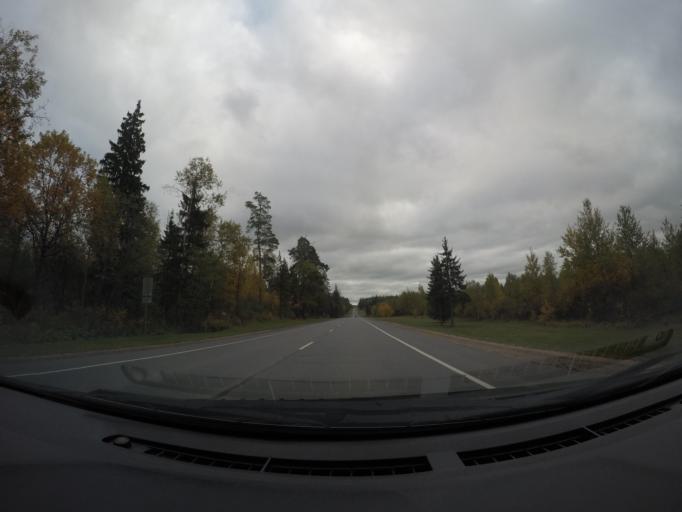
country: RU
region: Moskovskaya
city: Dorokhovo
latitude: 55.6189
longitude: 36.3456
